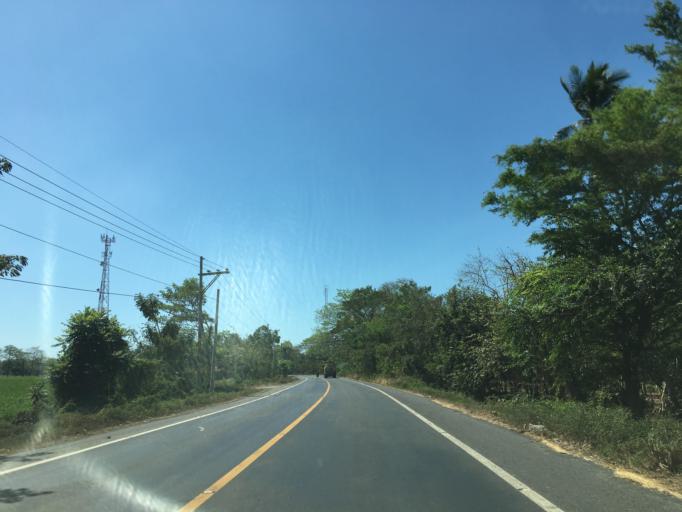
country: GT
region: Escuintla
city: Puerto San Jose
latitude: 13.9972
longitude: -90.8944
